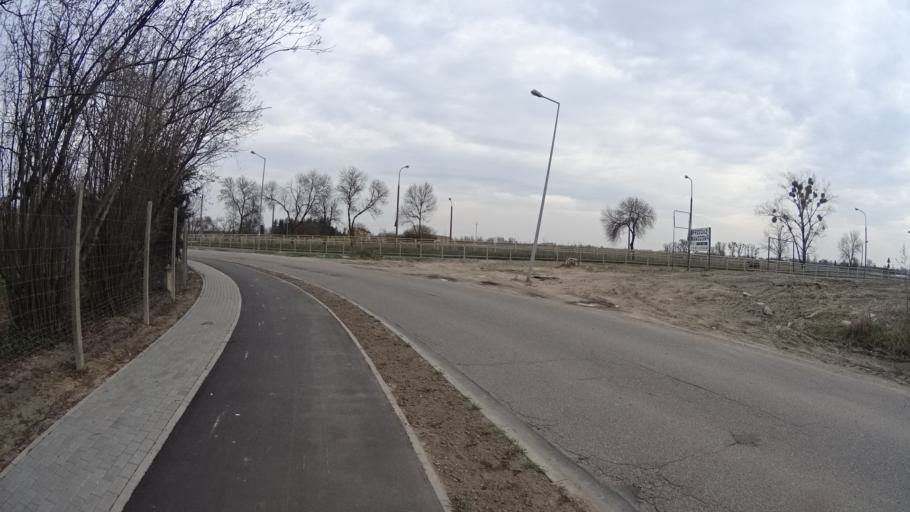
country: PL
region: Masovian Voivodeship
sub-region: Powiat warszawski zachodni
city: Jozefow
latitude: 52.2087
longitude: 20.6580
